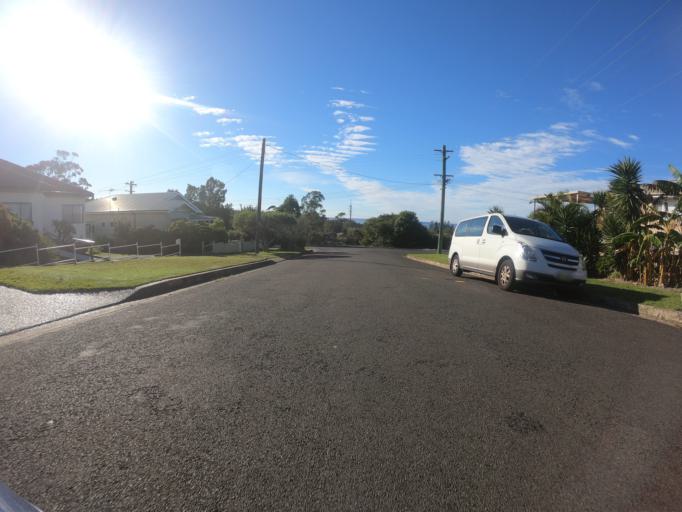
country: AU
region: New South Wales
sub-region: Wollongong
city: Bulli
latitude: -34.3129
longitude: 150.9215
